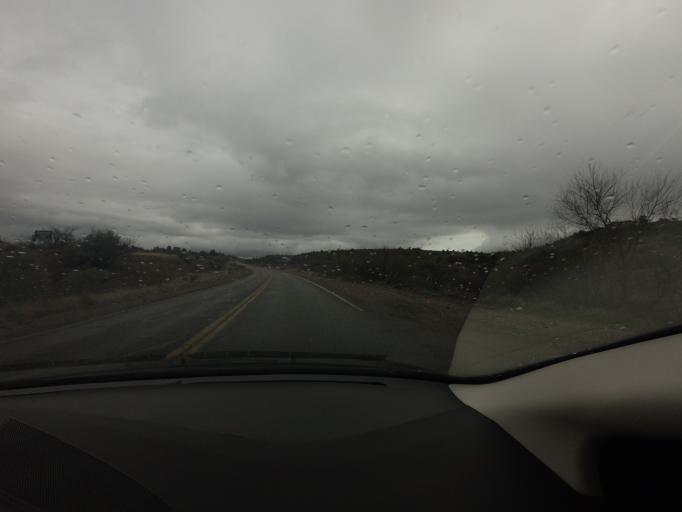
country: US
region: Arizona
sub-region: Yavapai County
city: Clarkdale
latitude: 34.7649
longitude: -112.0445
